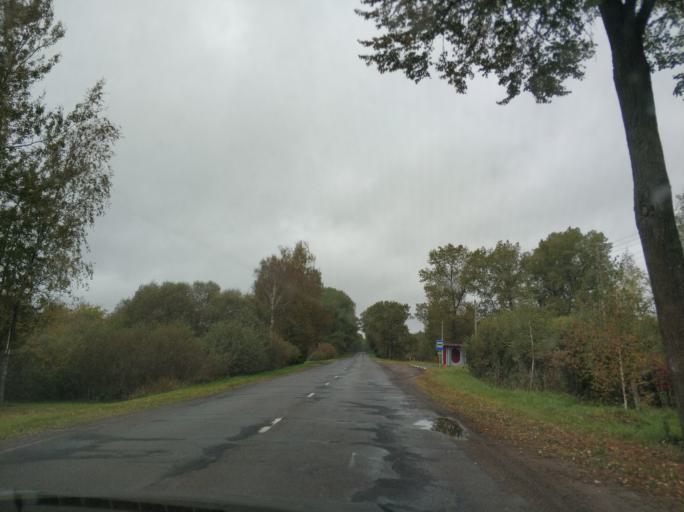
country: BY
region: Vitebsk
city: Polatsk
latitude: 55.4310
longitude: 28.9946
